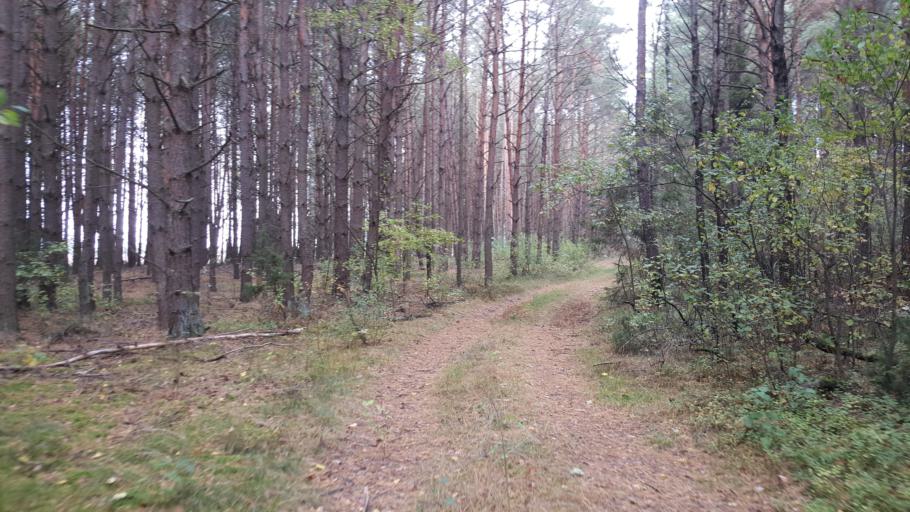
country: BY
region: Brest
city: Kamyanyets
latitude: 52.4301
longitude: 23.9091
